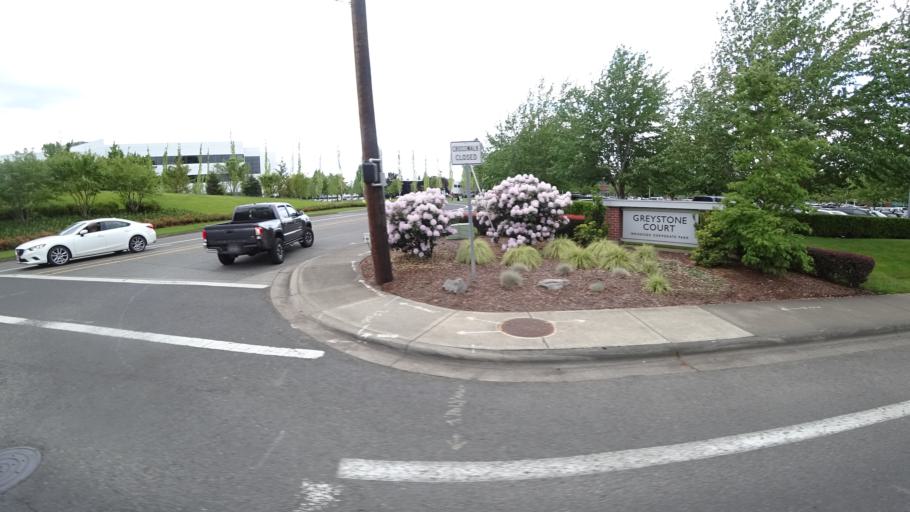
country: US
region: Oregon
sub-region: Washington County
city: Oak Hills
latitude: 45.5157
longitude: -122.8363
